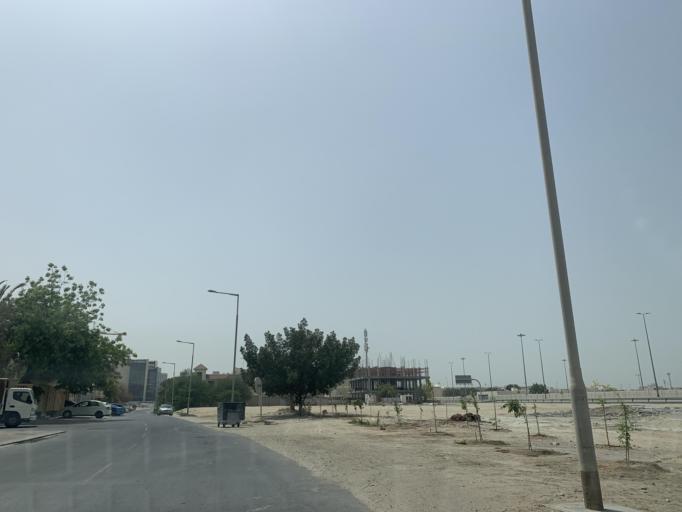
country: BH
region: Northern
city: Madinat `Isa
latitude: 26.1576
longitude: 50.5316
